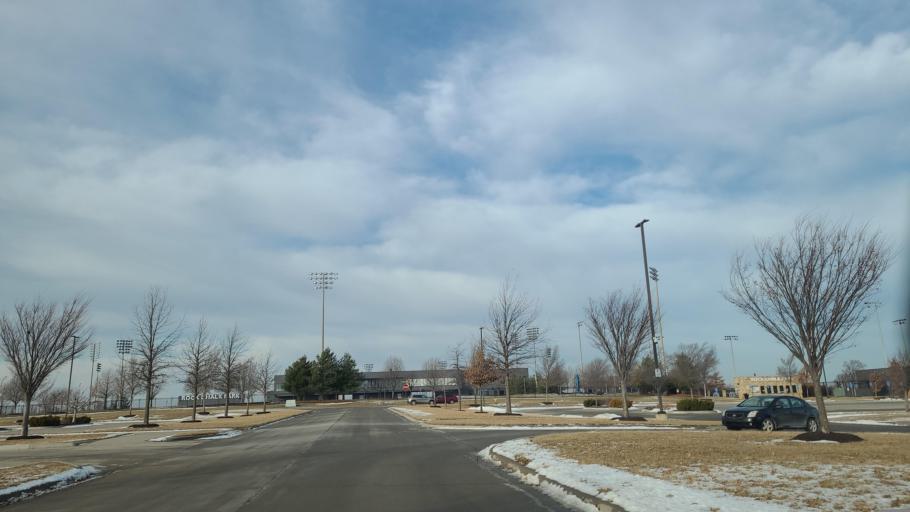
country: US
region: Kansas
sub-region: Douglas County
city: Lawrence
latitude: 38.9809
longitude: -95.3273
